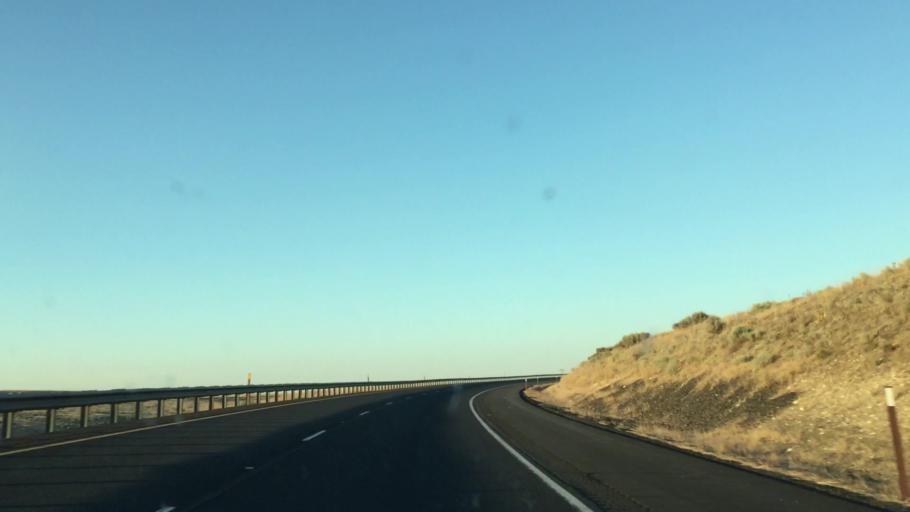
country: US
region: Washington
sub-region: Grant County
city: Quincy
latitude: 47.0040
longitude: -119.9704
